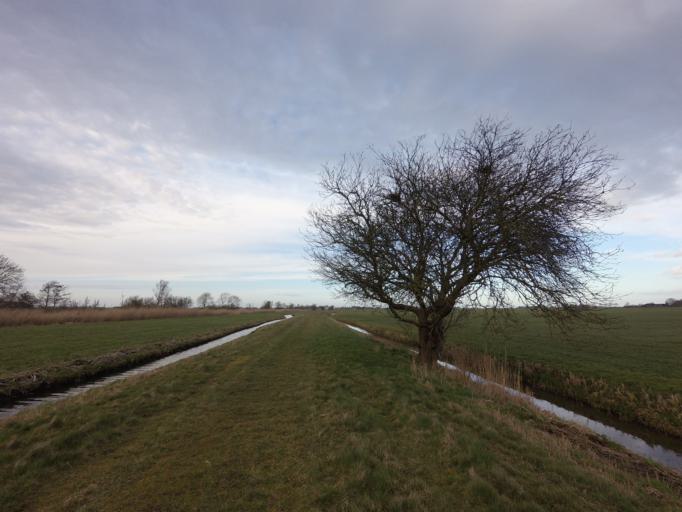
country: NL
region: Friesland
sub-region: Sudwest Fryslan
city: Bolsward
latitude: 53.0286
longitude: 5.4878
